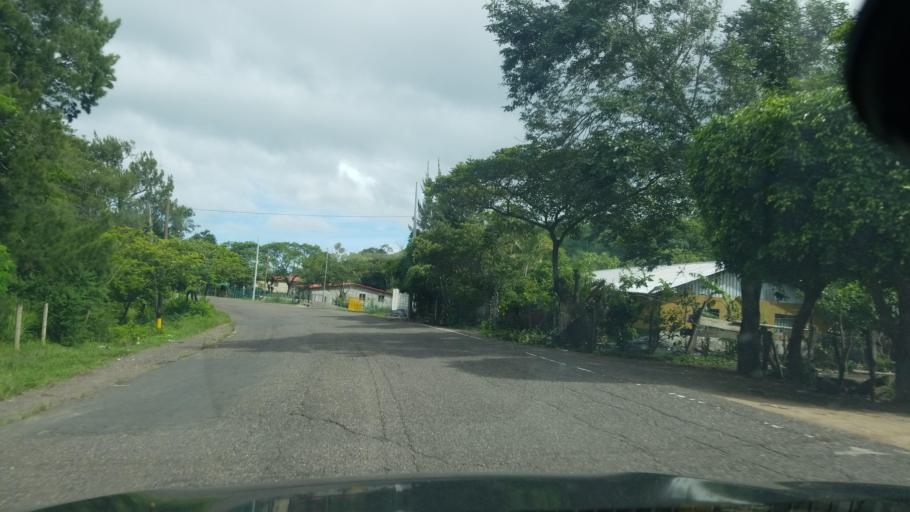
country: HN
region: Choluteca
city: Corpus
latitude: 13.3713
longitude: -86.9607
